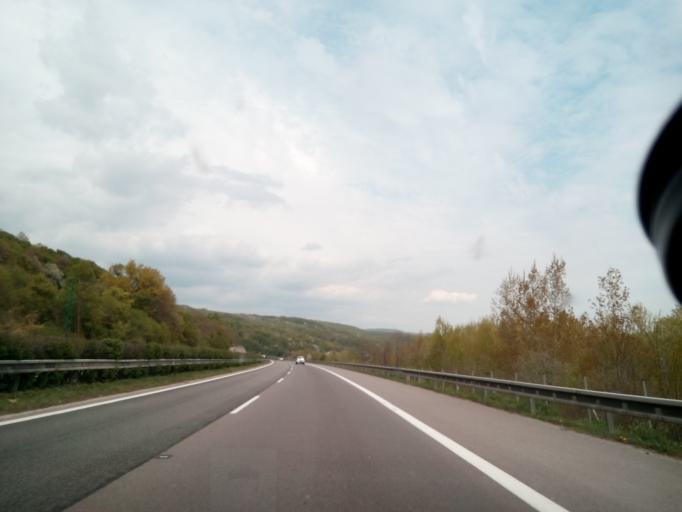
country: SK
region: Trenciansky
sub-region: Okres Trencin
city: Trencin
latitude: 48.8852
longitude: 17.9816
